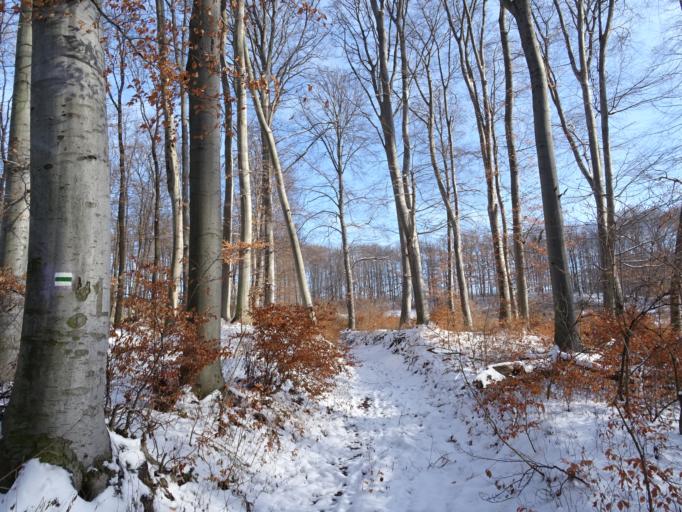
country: HU
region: Fejer
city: Mor
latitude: 47.3817
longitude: 18.2444
